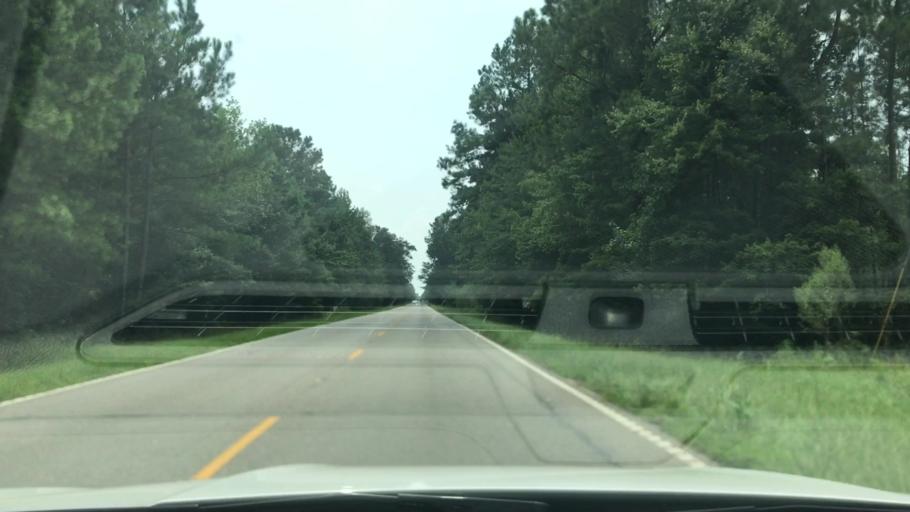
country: US
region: South Carolina
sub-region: Georgetown County
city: Murrells Inlet
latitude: 33.5517
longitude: -79.2197
